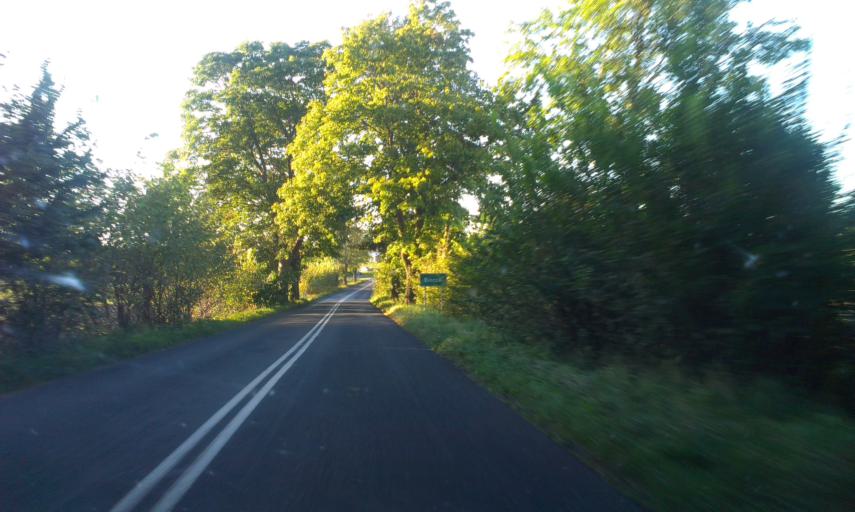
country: PL
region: Pomeranian Voivodeship
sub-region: Powiat czluchowski
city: Rzeczenica
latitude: 53.6439
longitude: 17.1477
